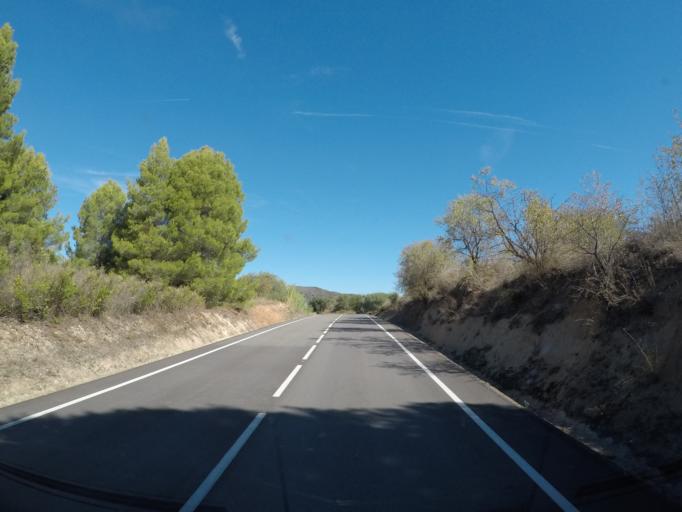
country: ES
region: Catalonia
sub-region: Provincia de Tarragona
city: Falset
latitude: 41.1521
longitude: 0.8179
